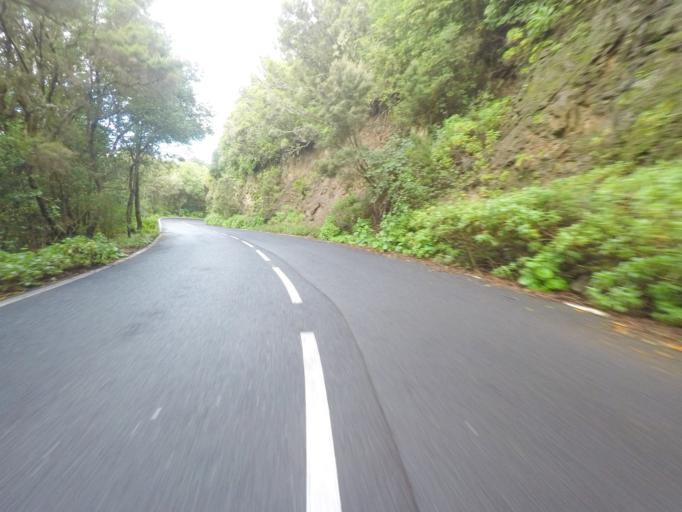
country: ES
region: Canary Islands
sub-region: Provincia de Santa Cruz de Tenerife
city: Hermigua
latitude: 28.1208
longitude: -17.2175
